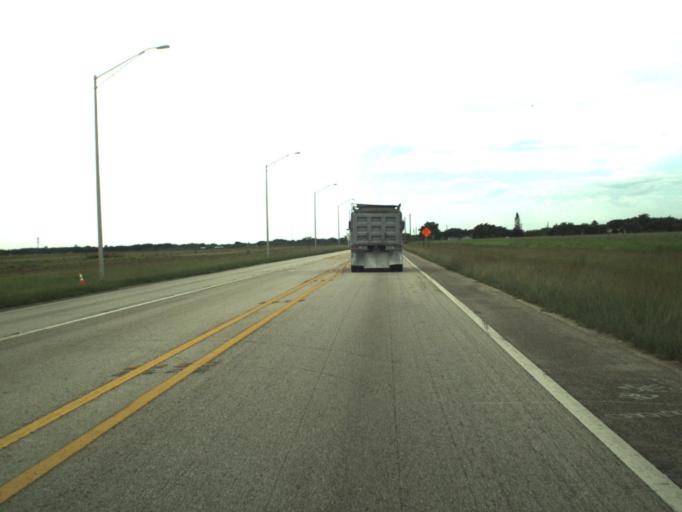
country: US
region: Florida
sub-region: Miami-Dade County
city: Country Walk
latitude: 25.6372
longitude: -80.4799
